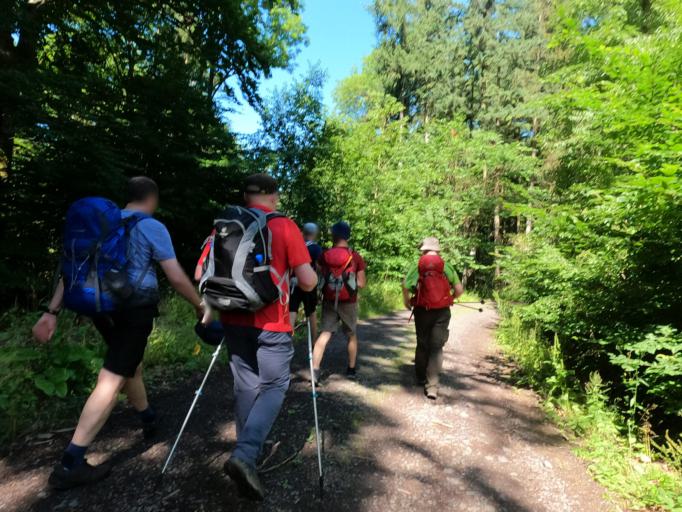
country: DE
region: Bavaria
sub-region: Regierungsbezirk Unterfranken
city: Zeitlofs
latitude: 50.3334
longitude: 9.6325
